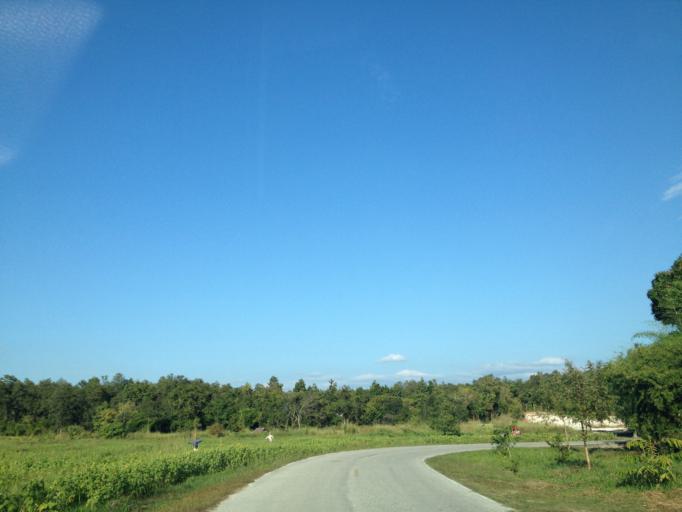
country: TH
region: Chiang Mai
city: Chiang Mai
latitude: 18.8721
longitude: 98.9370
